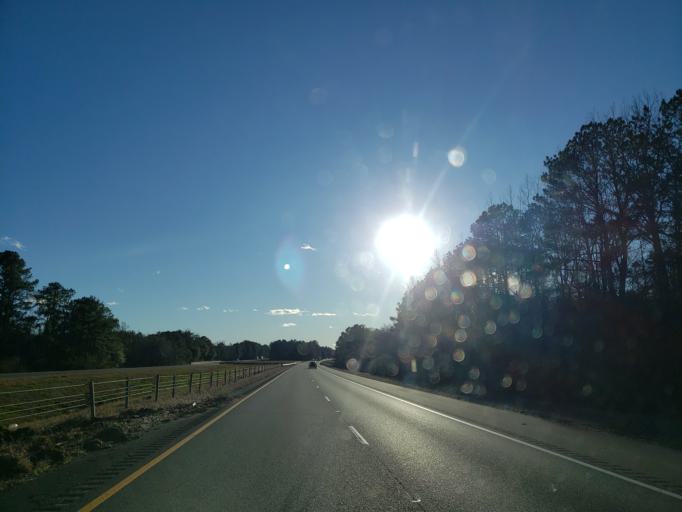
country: US
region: Alabama
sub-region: Hale County
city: Moundville
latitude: 33.0128
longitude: -87.7569
